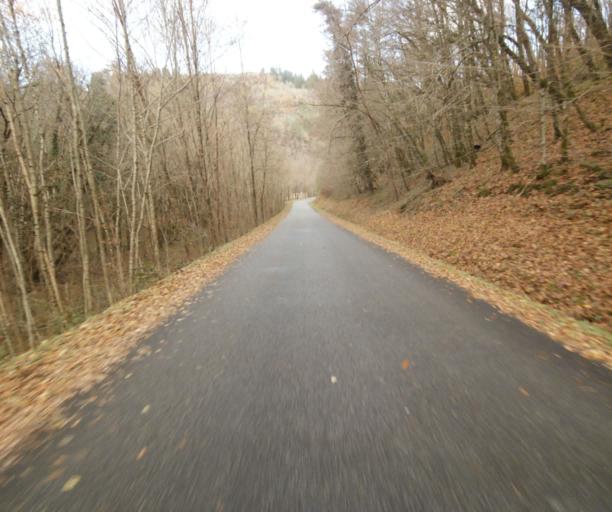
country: FR
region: Limousin
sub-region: Departement de la Correze
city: Laguenne
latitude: 45.2384
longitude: 1.7847
